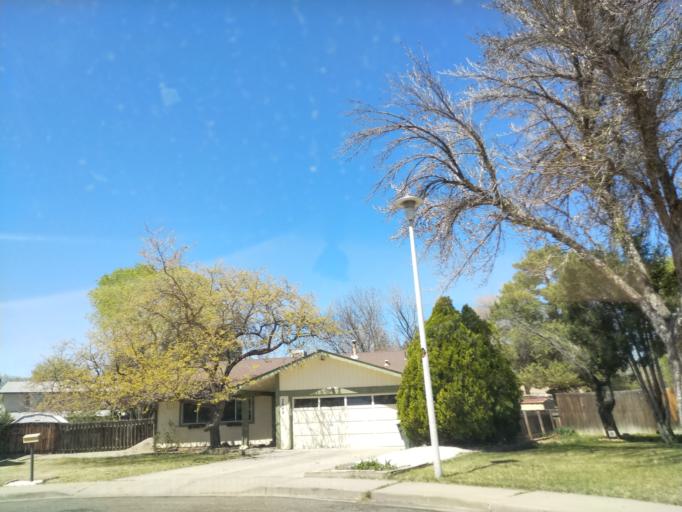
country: US
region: Colorado
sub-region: Mesa County
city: Grand Junction
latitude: 39.0937
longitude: -108.5398
